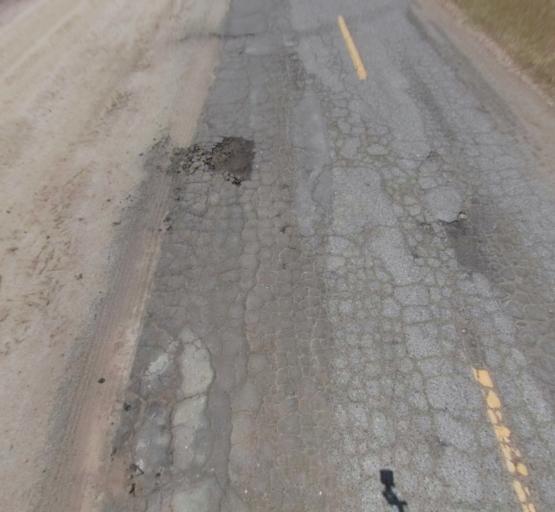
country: US
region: California
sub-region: Madera County
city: Chowchilla
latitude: 37.0820
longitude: -120.4190
